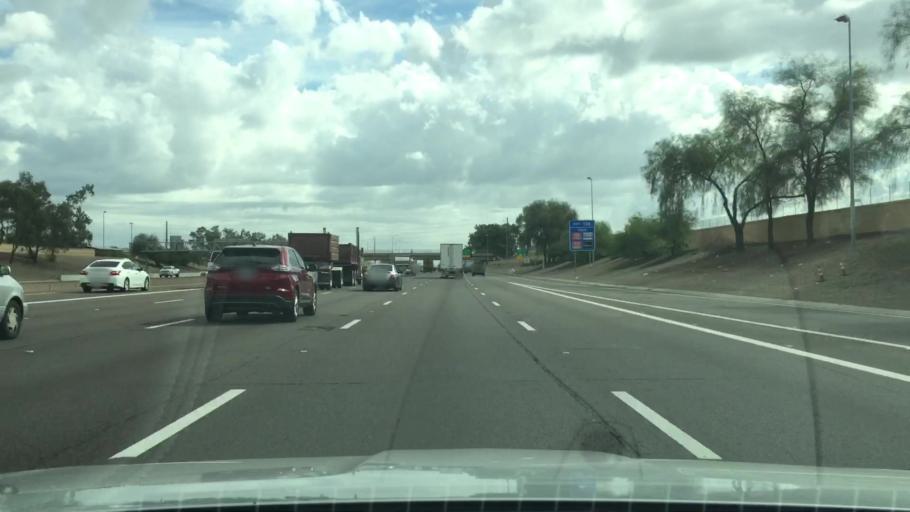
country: US
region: Arizona
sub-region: Maricopa County
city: Tolleson
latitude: 33.4618
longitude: -112.2335
